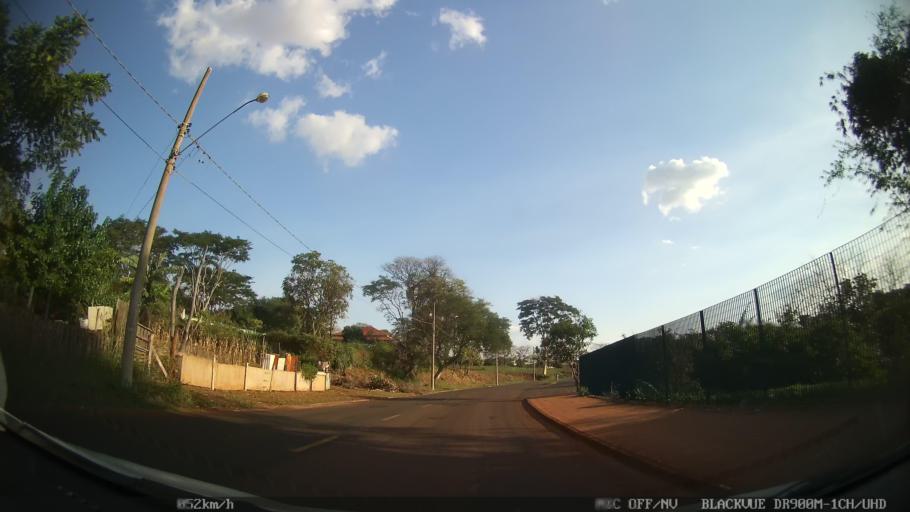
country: BR
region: Sao Paulo
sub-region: Ribeirao Preto
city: Ribeirao Preto
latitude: -21.1517
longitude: -47.8399
